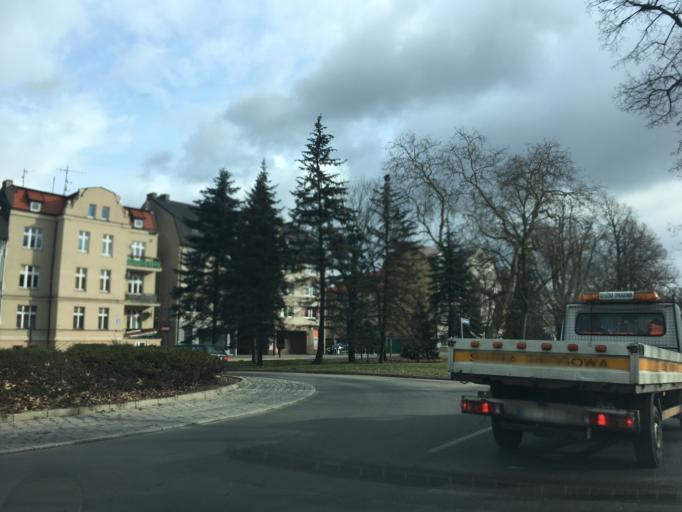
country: PL
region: Pomeranian Voivodeship
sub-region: Slupsk
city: Slupsk
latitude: 54.4705
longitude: 17.0275
